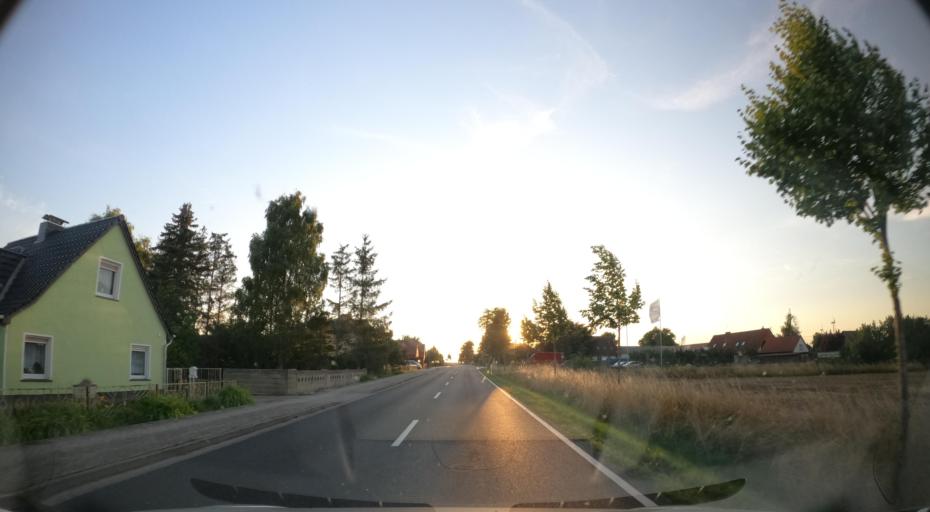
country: DE
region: Mecklenburg-Vorpommern
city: Strasburg
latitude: 53.4915
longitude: 13.8081
